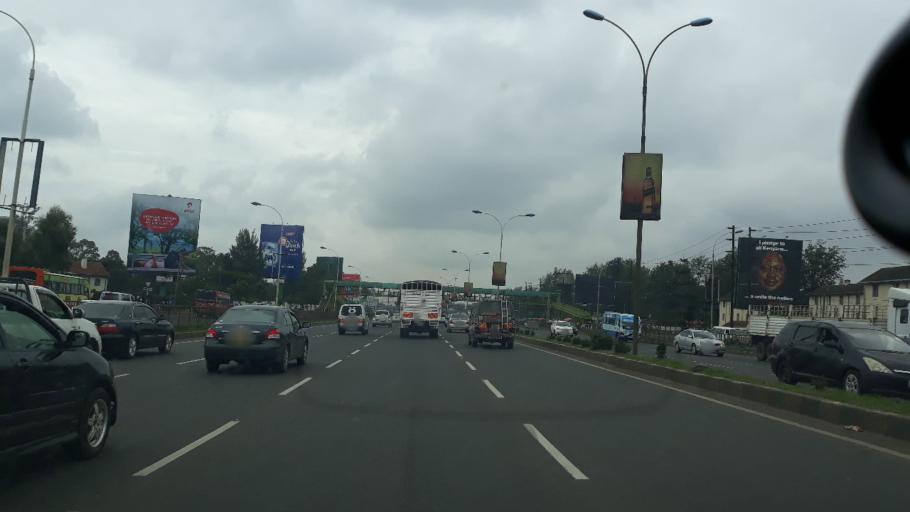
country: KE
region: Nairobi Area
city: Pumwani
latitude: -1.2603
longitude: 36.8429
